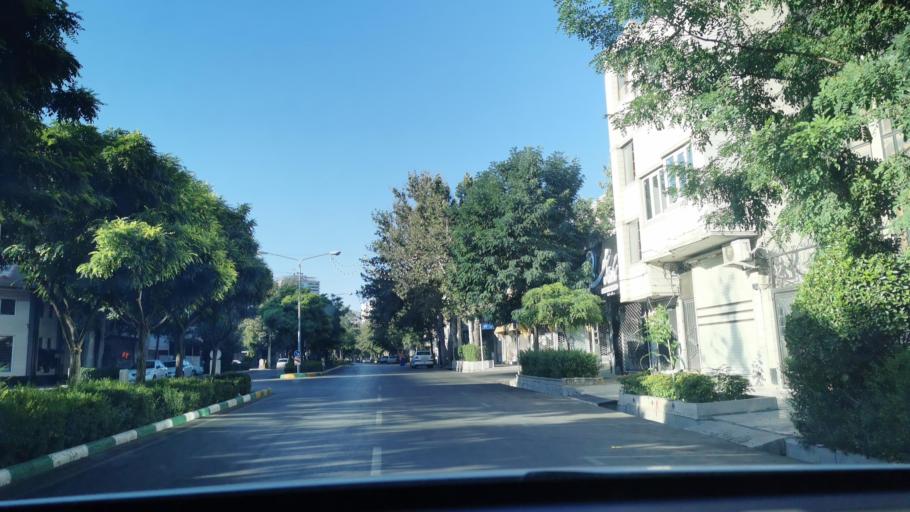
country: IR
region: Razavi Khorasan
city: Mashhad
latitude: 36.2915
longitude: 59.5675
